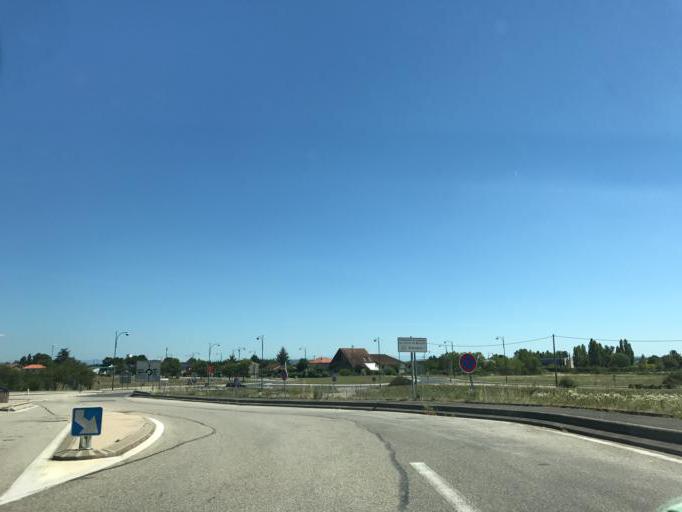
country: FR
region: Rhone-Alpes
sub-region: Departement de l'Ain
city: Balan
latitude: 45.8508
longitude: 5.0999
